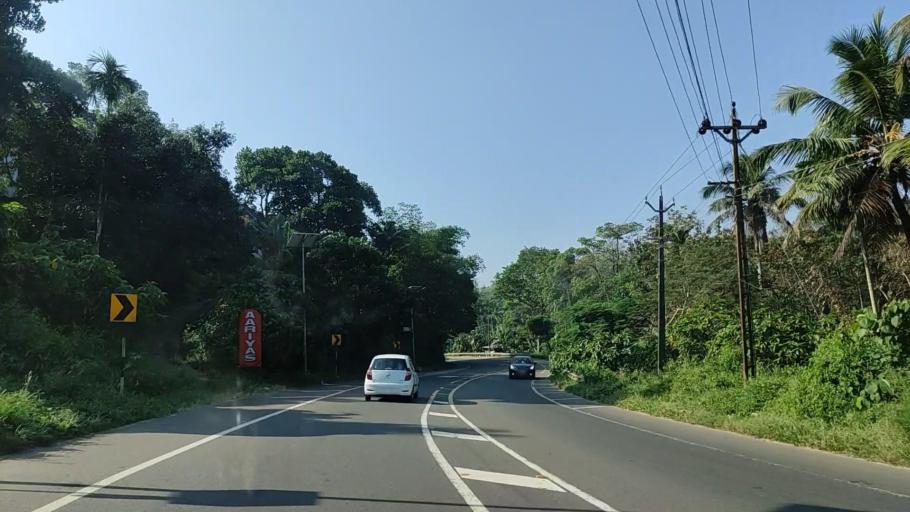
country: IN
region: Kerala
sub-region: Kollam
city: Punalur
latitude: 8.9082
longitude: 76.8549
